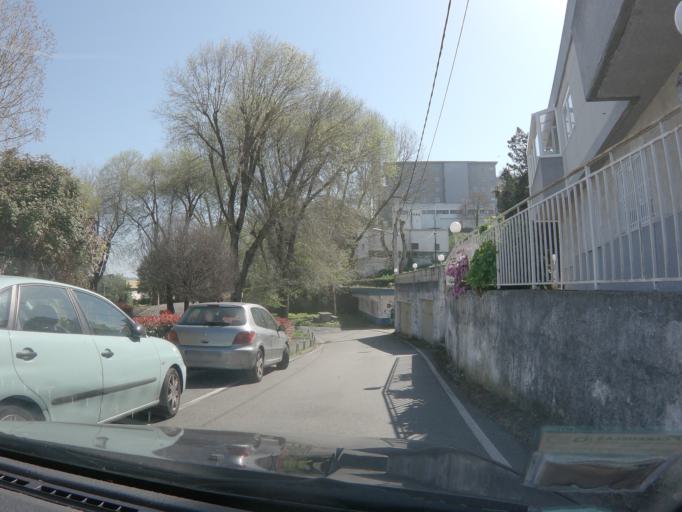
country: ES
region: Galicia
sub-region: Provincia da Coruna
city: A Coruna
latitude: 43.3404
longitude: -8.3882
